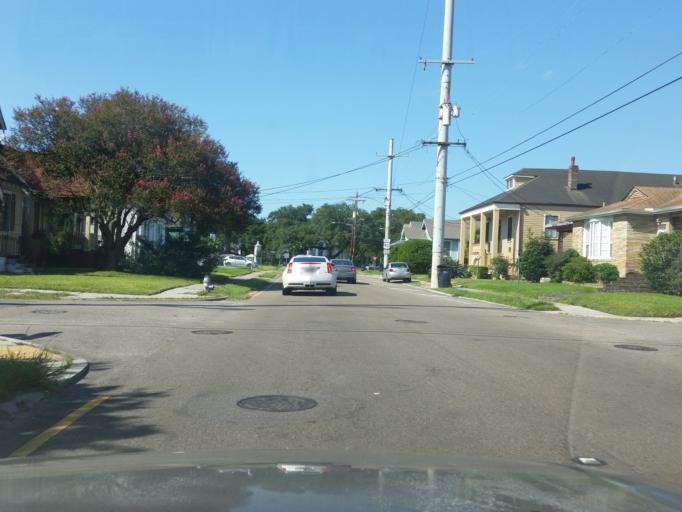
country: US
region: Louisiana
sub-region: Orleans Parish
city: New Orleans
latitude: 29.9924
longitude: -90.0658
